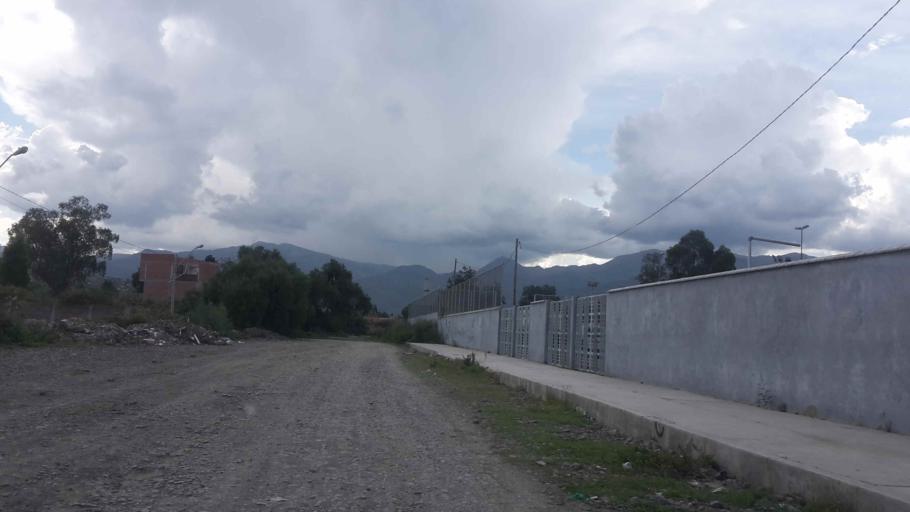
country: BO
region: Cochabamba
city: Sipe Sipe
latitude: -17.4087
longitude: -66.2897
